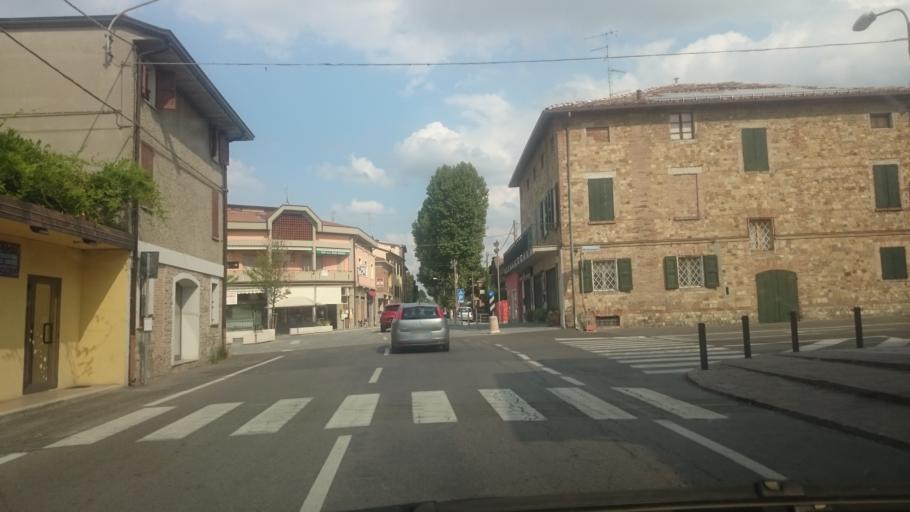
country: IT
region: Emilia-Romagna
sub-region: Provincia di Reggio Emilia
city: Salvaterra
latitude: 44.6013
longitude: 10.7669
